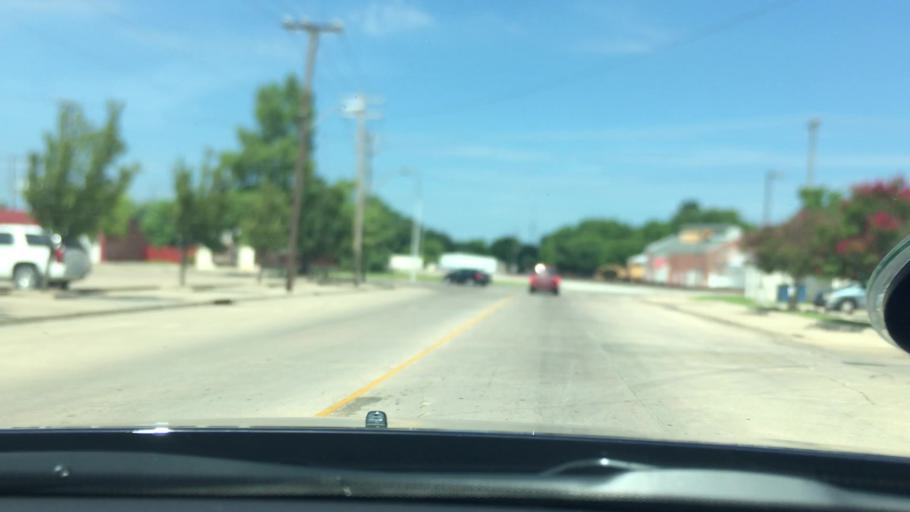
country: US
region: Oklahoma
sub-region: Pontotoc County
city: Ada
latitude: 34.7756
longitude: -96.6794
